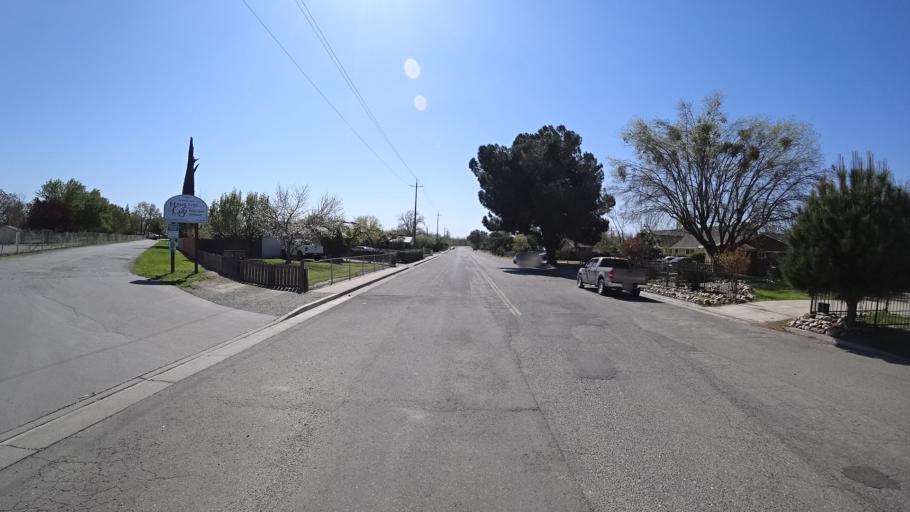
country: US
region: California
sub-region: Glenn County
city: Hamilton City
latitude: 39.7426
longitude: -122.0070
